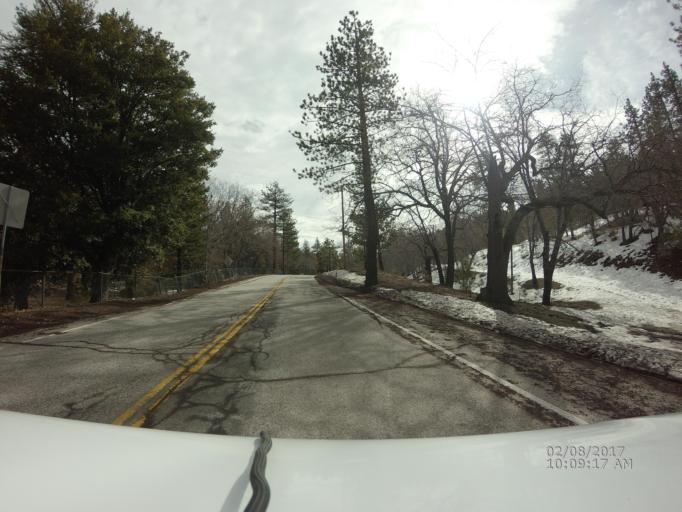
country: US
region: California
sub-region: San Bernardino County
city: Pinon Hills
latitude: 34.3946
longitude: -117.7303
